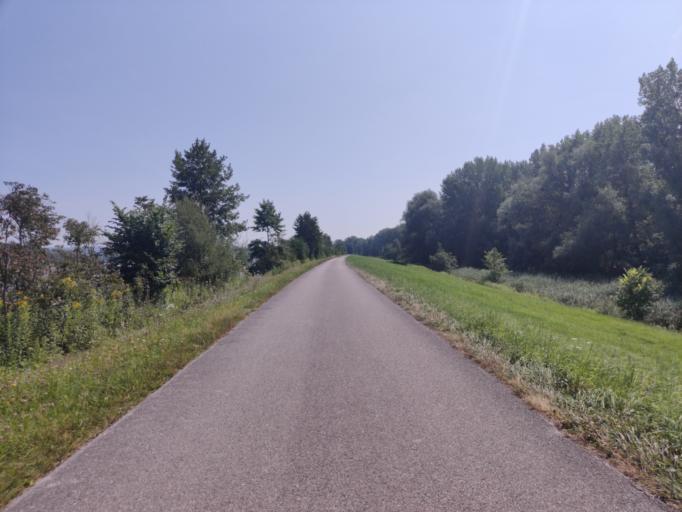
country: AT
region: Upper Austria
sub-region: Politischer Bezirk Urfahr-Umgebung
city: Goldworth
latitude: 48.3119
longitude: 14.1006
